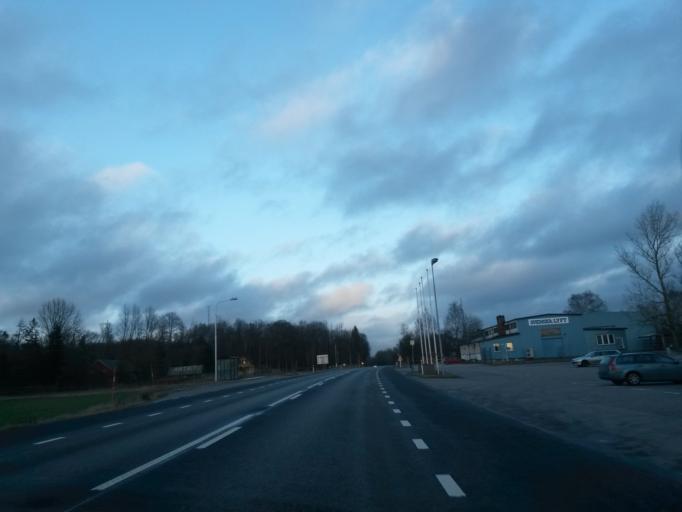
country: SE
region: Halland
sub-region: Halmstads Kommun
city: Aled
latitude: 56.7464
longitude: 12.9325
